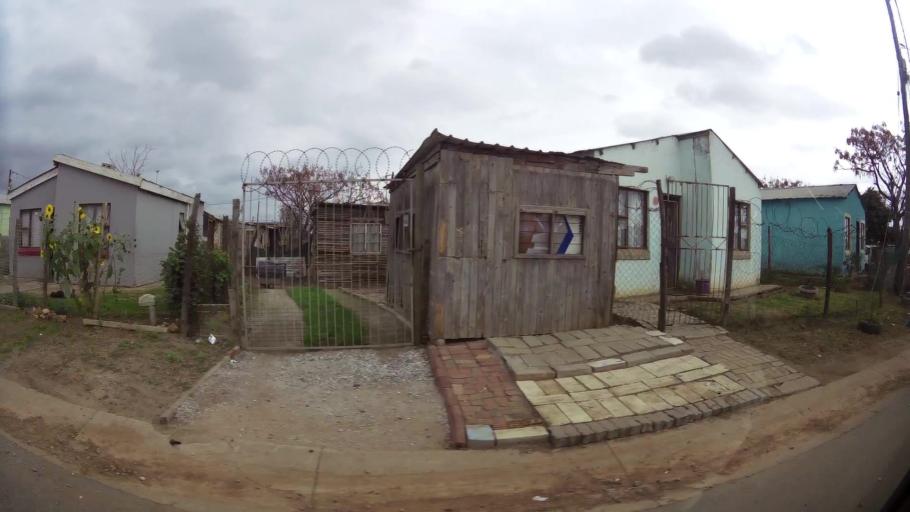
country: ZA
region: Eastern Cape
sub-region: Nelson Mandela Bay Metropolitan Municipality
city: Port Elizabeth
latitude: -33.8884
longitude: 25.5542
